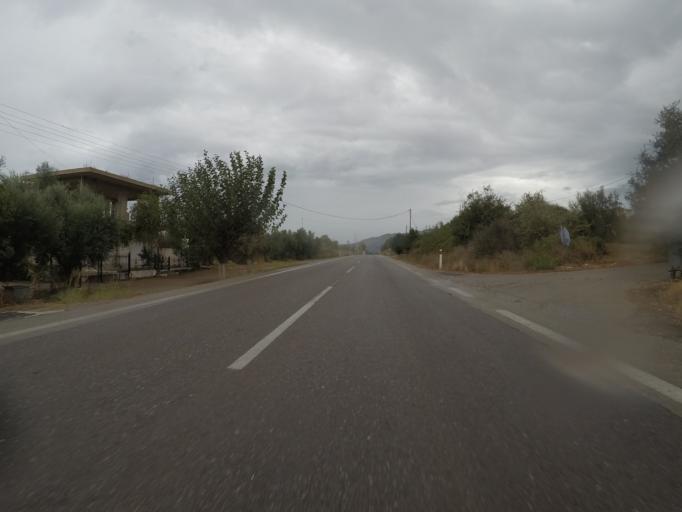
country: GR
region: West Greece
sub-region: Nomos Ileias
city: Zacharo
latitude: 37.4330
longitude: 21.6639
